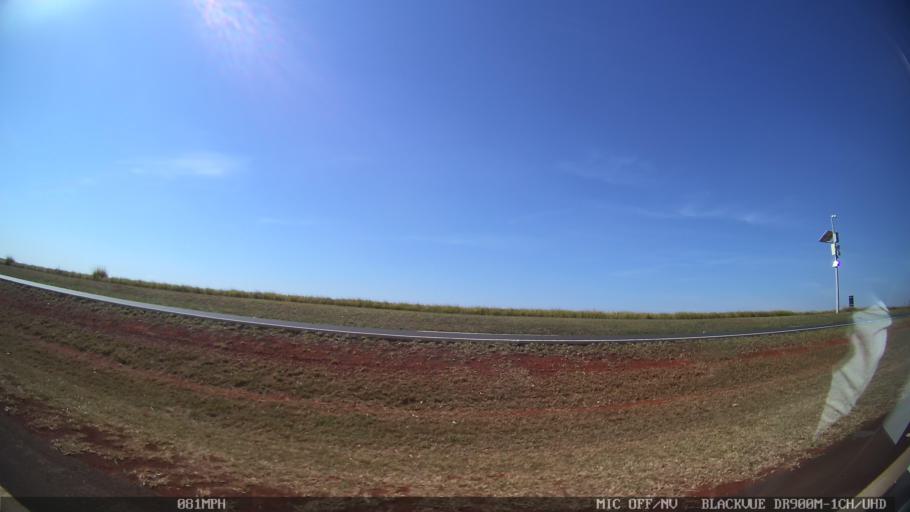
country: BR
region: Sao Paulo
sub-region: Ribeirao Preto
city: Ribeirao Preto
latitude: -21.1813
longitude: -47.8919
